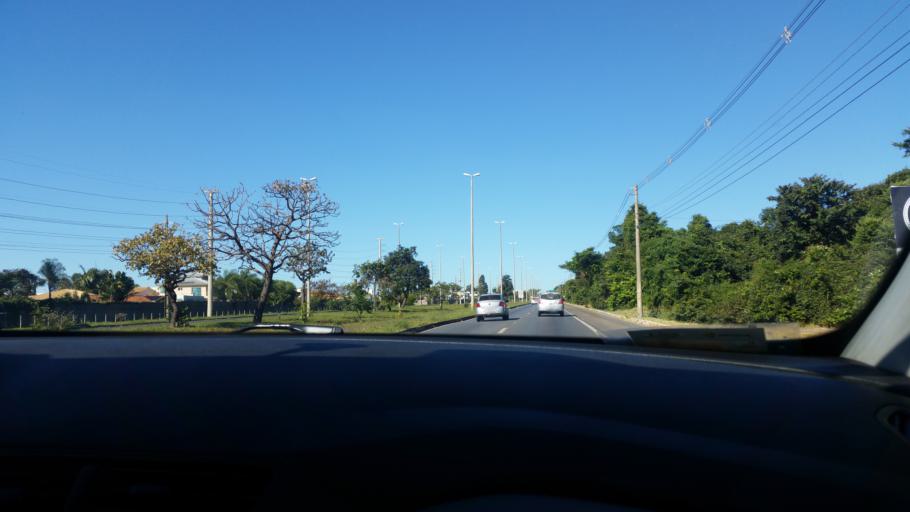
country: BR
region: Federal District
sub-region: Brasilia
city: Brasilia
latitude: -15.8560
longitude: -47.8179
